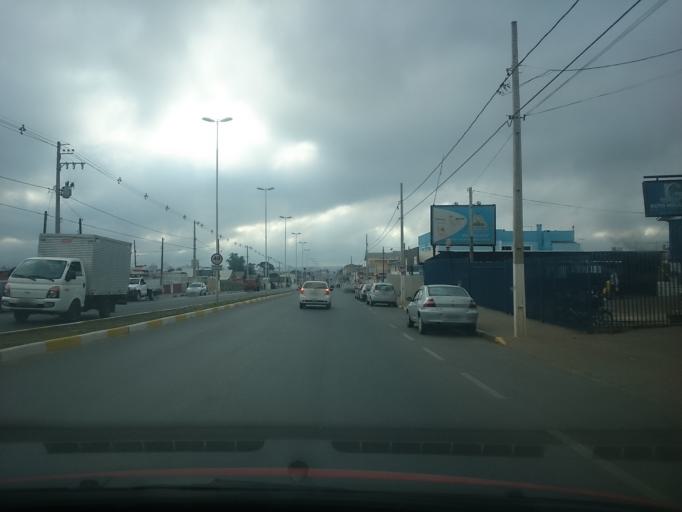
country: BR
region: Santa Catarina
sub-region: Lages
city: Lages
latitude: -27.8320
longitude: -50.3459
